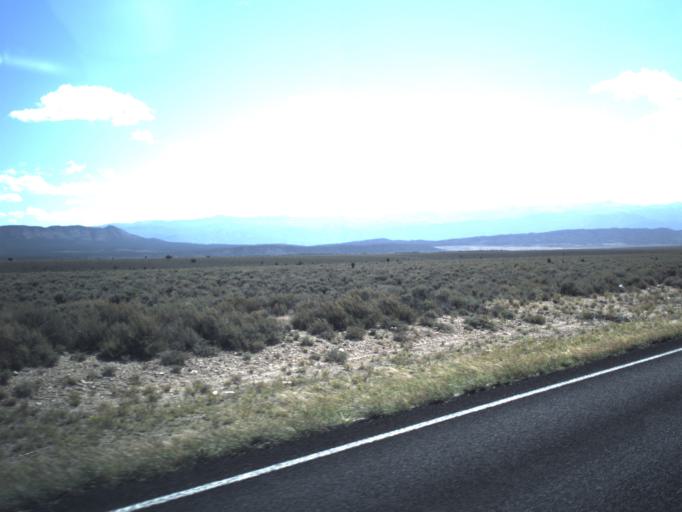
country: US
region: Utah
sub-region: Iron County
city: Parowan
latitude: 38.0161
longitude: -112.9980
